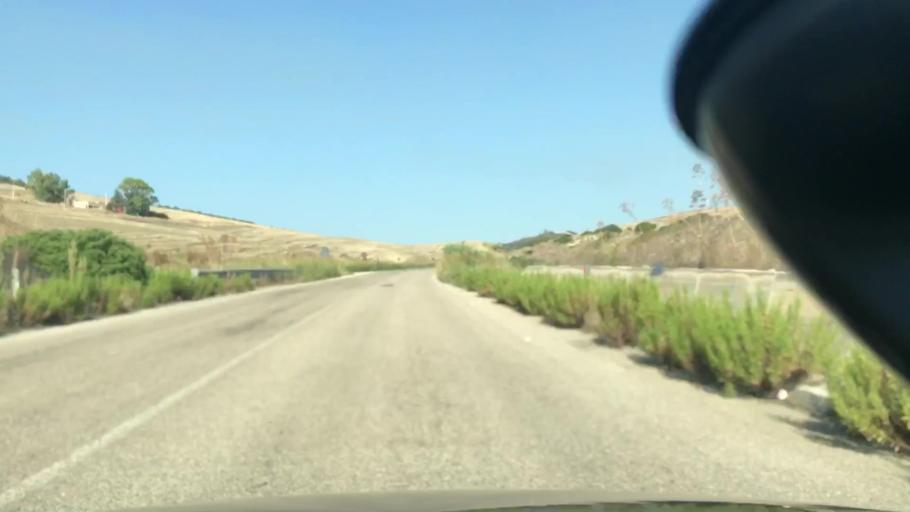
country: IT
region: Basilicate
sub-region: Provincia di Matera
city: Grottole
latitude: 40.6938
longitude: 16.4299
